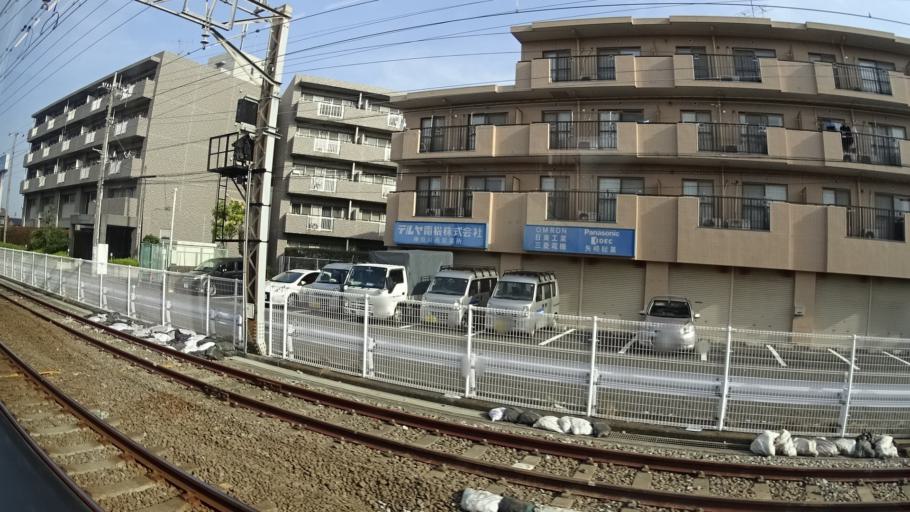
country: JP
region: Kanagawa
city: Minami-rinkan
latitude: 35.4711
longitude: 139.4376
